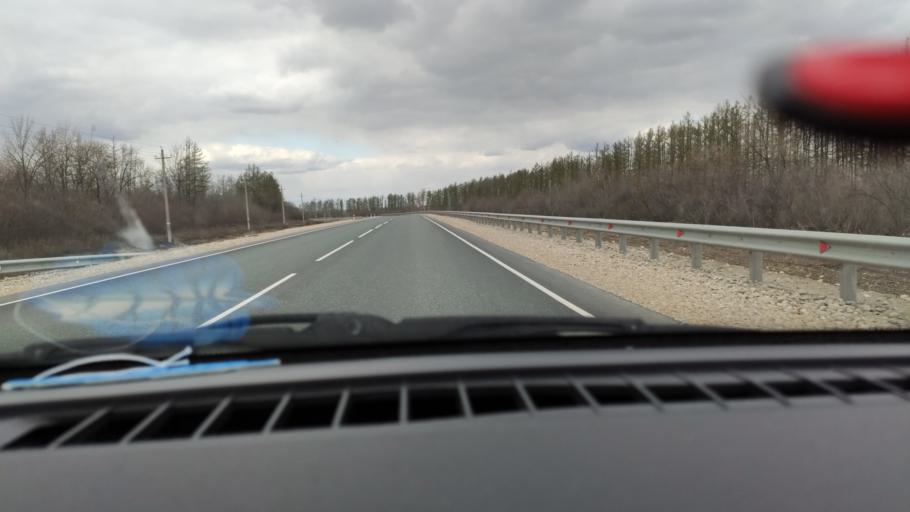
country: RU
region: Saratov
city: Shikhany
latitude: 52.1615
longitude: 47.1641
